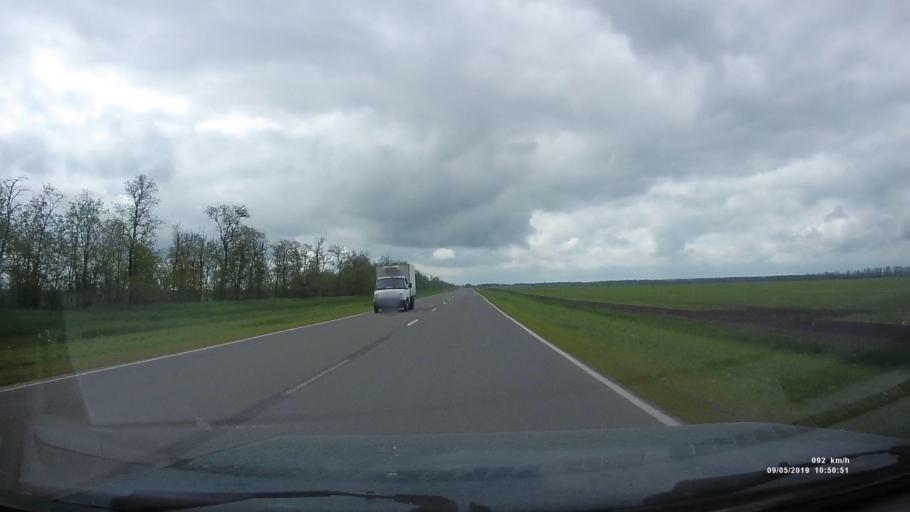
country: RU
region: Rostov
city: Peshkovo
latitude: 46.9229
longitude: 39.3553
